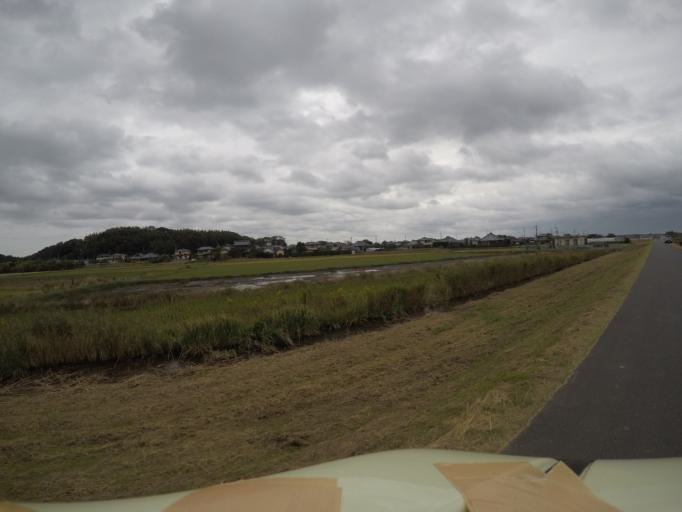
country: JP
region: Ibaraki
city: Ishioka
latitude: 36.1003
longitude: 140.3751
